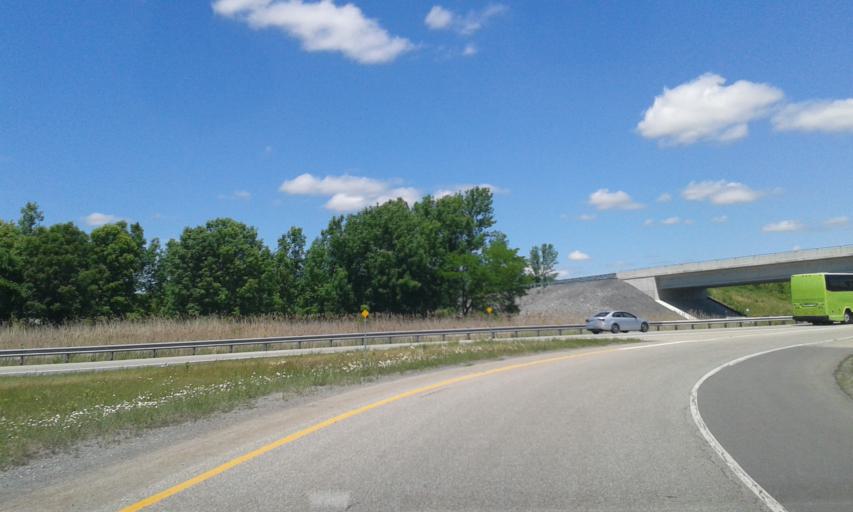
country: US
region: New York
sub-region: St. Lawrence County
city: Massena
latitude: 45.0457
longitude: -74.9075
